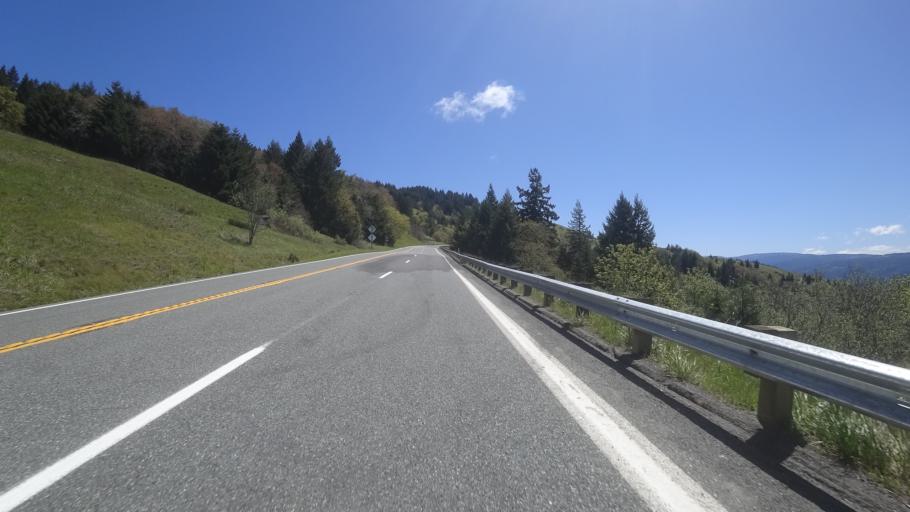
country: US
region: California
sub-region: Humboldt County
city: Willow Creek
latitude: 40.9089
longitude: -123.7848
